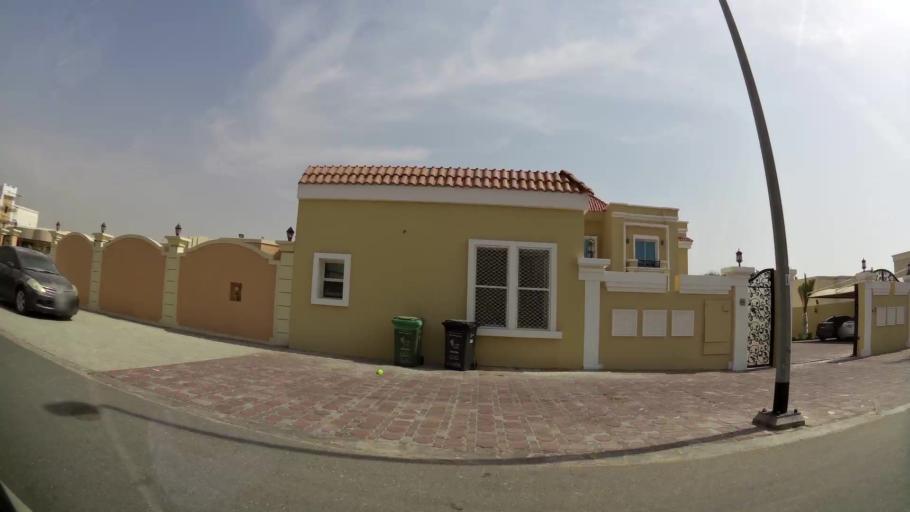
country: AE
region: Ash Shariqah
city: Sharjah
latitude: 25.2487
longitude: 55.4426
